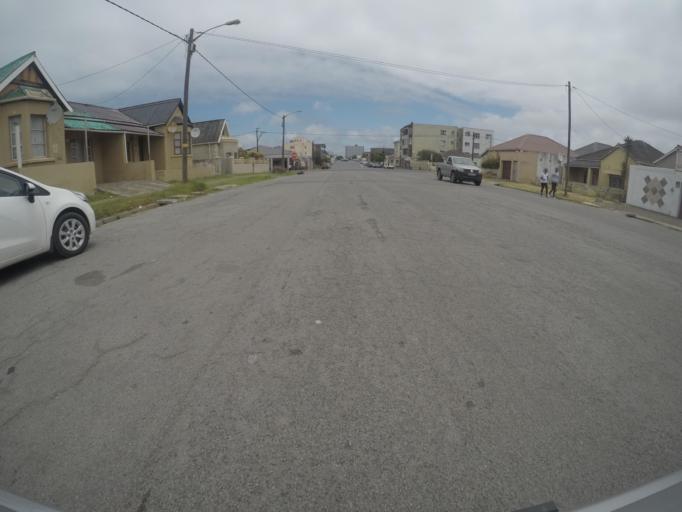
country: ZA
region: Eastern Cape
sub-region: Buffalo City Metropolitan Municipality
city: East London
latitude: -33.0153
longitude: 27.9165
